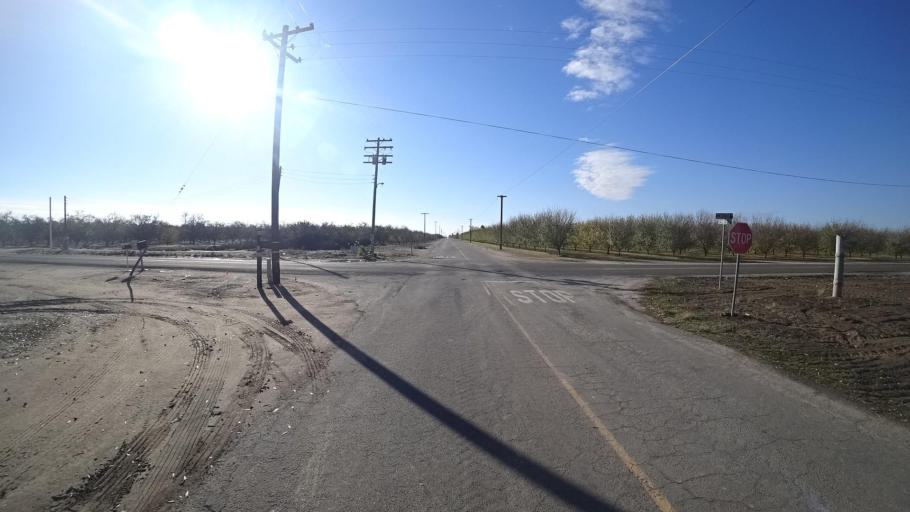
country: US
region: California
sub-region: Kern County
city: Delano
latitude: 35.7324
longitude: -119.3119
